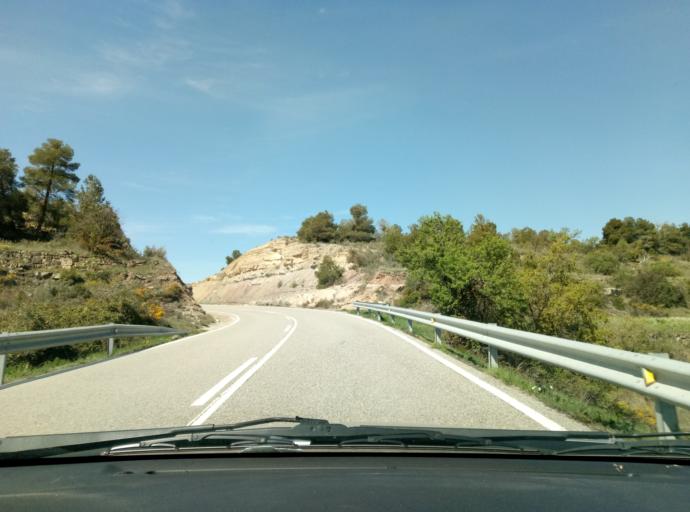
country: ES
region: Catalonia
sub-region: Provincia de Lleida
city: Fulleda
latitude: 41.5110
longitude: 1.0229
